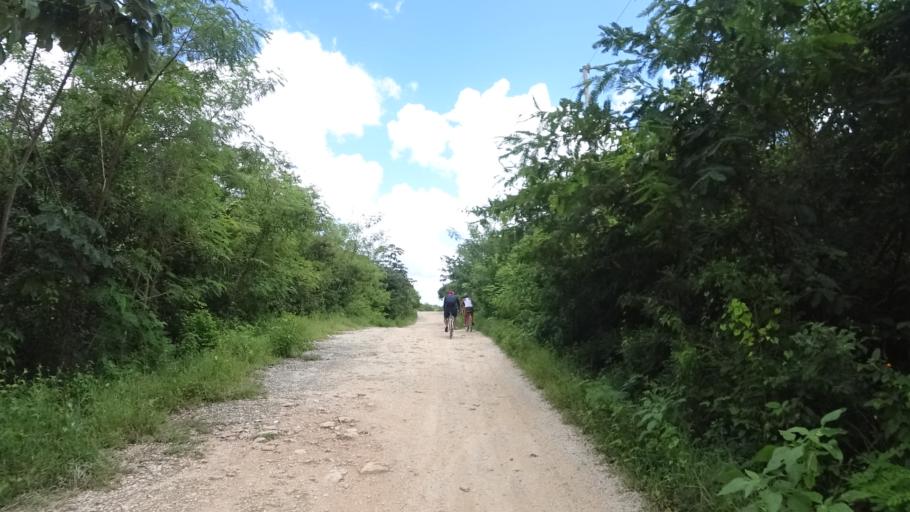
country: MX
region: Yucatan
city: Valladolid
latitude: 20.6731
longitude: -88.2264
